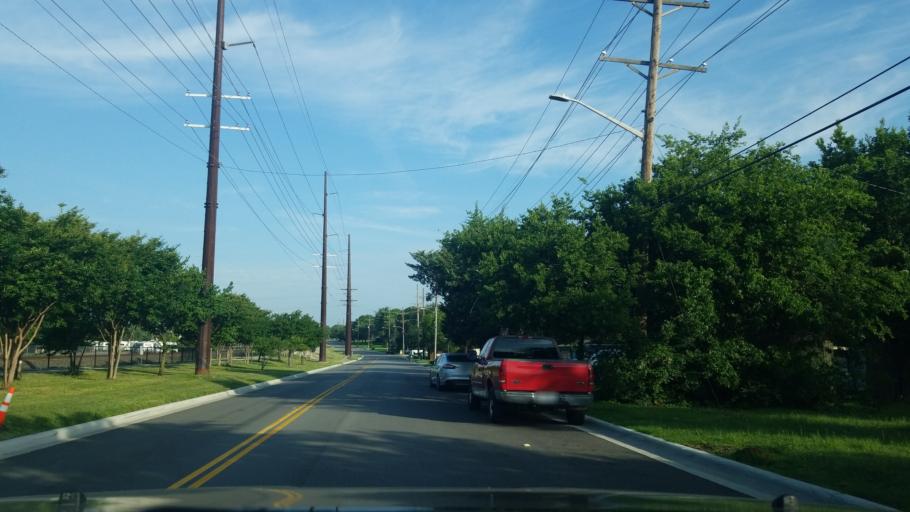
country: US
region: Texas
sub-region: Denton County
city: Denton
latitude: 33.2020
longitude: -97.1168
